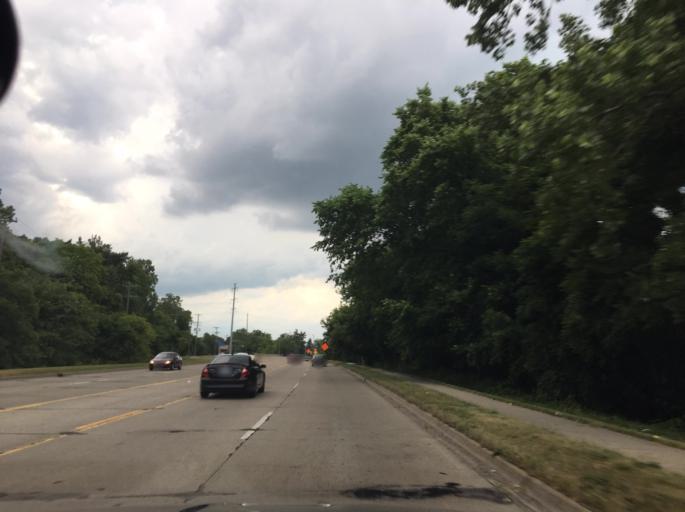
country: US
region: Michigan
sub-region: Macomb County
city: Clinton
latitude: 42.5756
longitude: -82.9513
